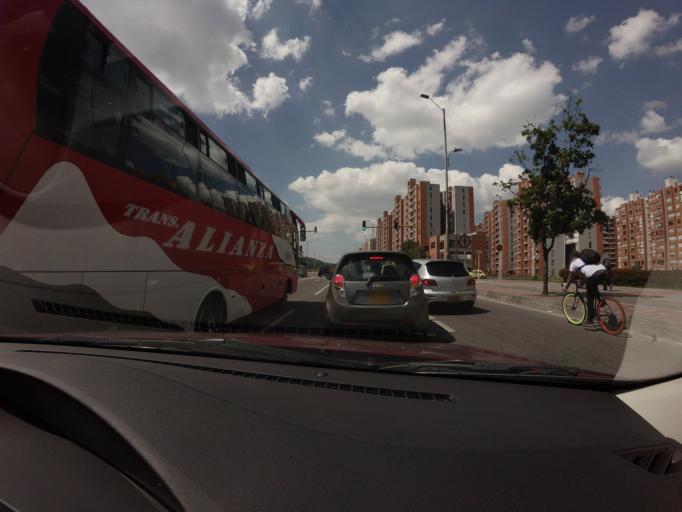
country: CO
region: Cundinamarca
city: Cota
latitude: 4.7420
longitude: -74.0651
